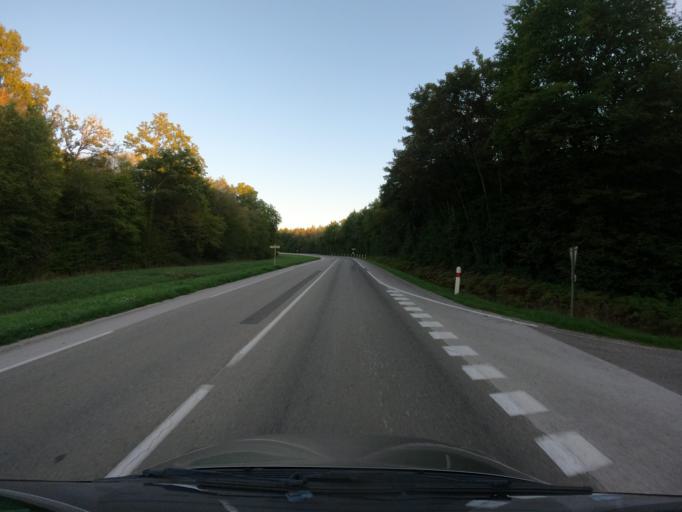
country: FR
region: Franche-Comte
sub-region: Departement du Jura
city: Montmorot
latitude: 46.7023
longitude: 5.4846
